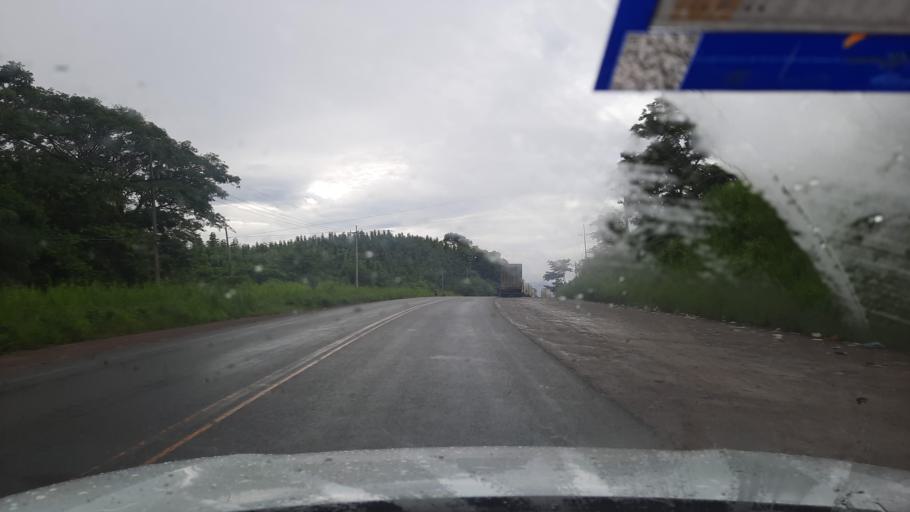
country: NI
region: Rivas
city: Cardenas
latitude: 11.1936
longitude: -85.6226
